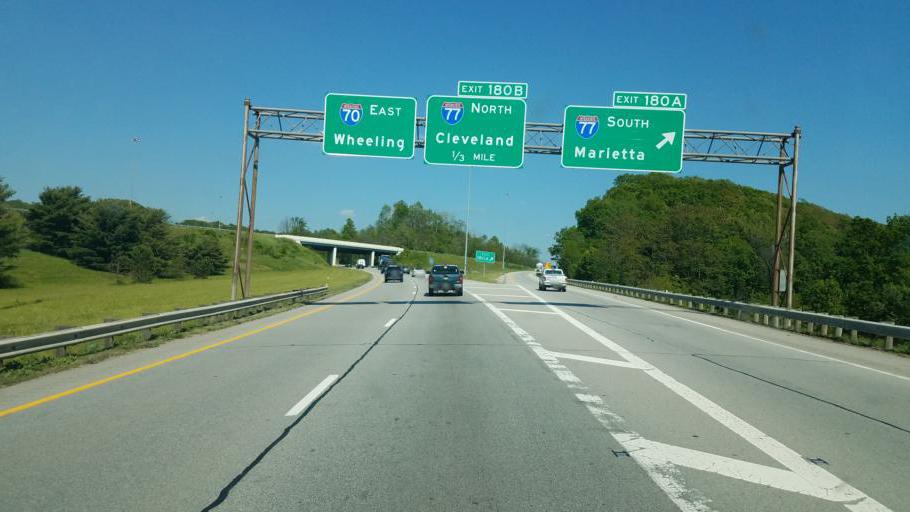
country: US
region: Ohio
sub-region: Guernsey County
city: Byesville
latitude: 39.9965
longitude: -81.5622
